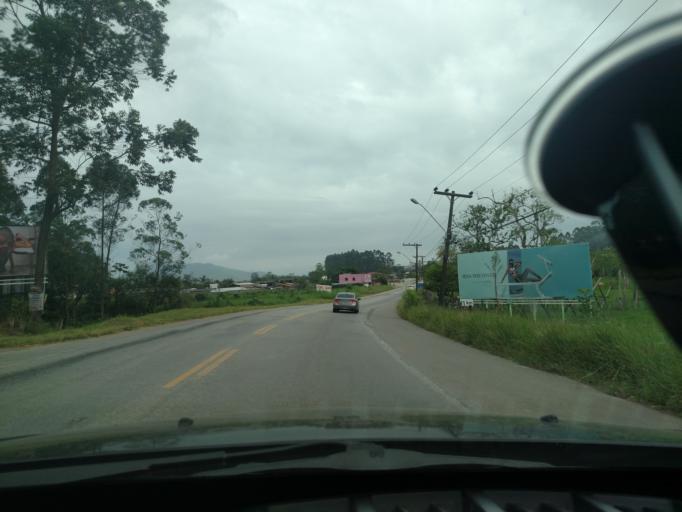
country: BR
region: Santa Catarina
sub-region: Itajai
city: Itajai
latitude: -26.8908
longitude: -48.7584
